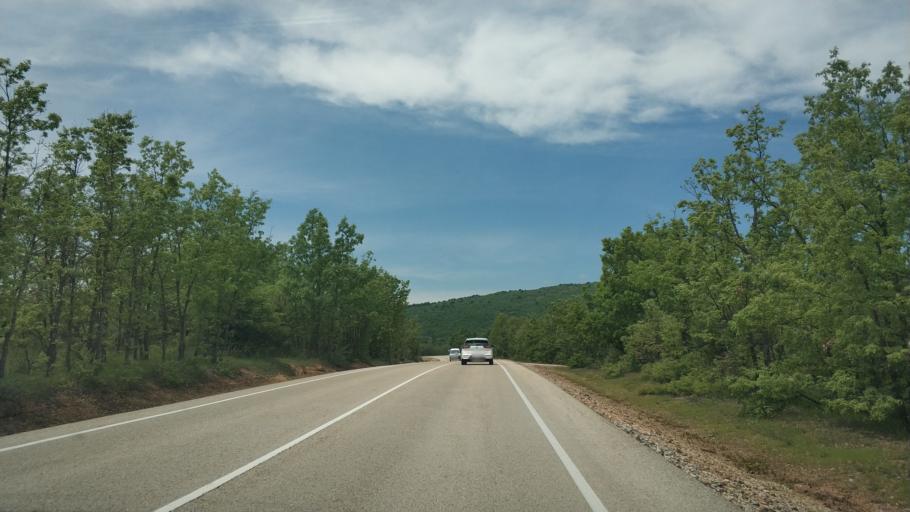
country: ES
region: Castille and Leon
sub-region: Provincia de Soria
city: Vinuesa
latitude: 41.8876
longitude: -2.6892
